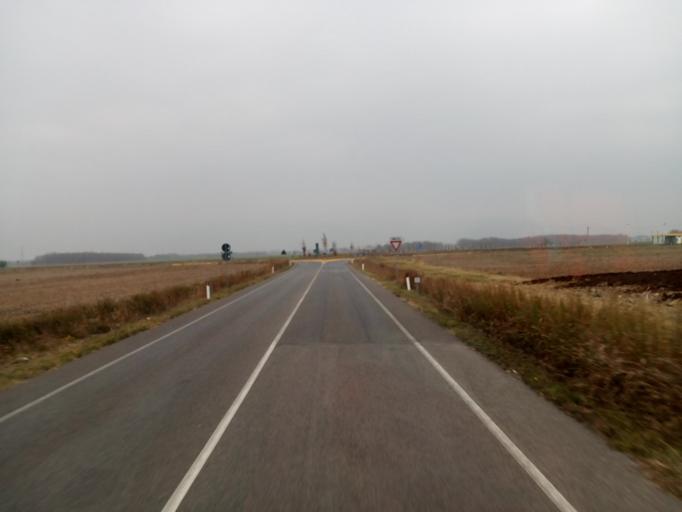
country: IT
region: Friuli Venezia Giulia
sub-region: Provincia di Udine
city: Premariacco
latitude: 46.0574
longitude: 13.3803
